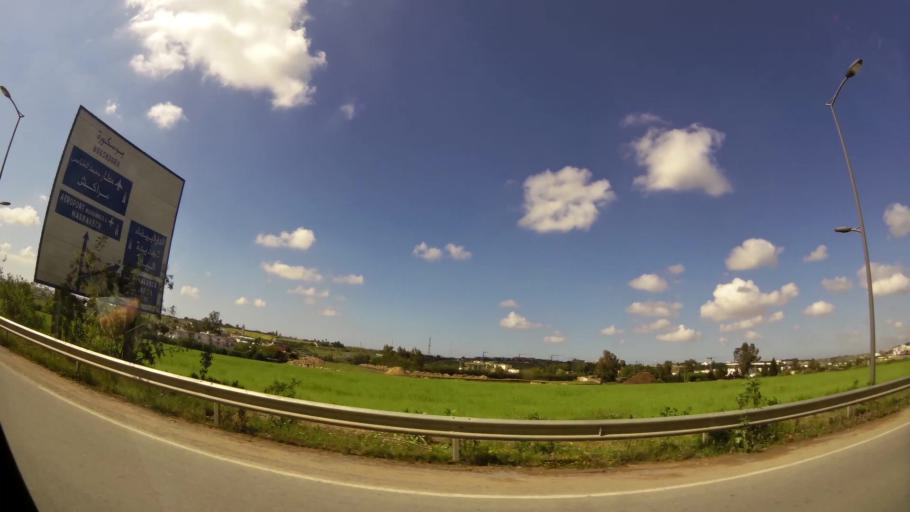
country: MA
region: Grand Casablanca
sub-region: Nouaceur
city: Bouskoura
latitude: 33.4825
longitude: -7.6279
